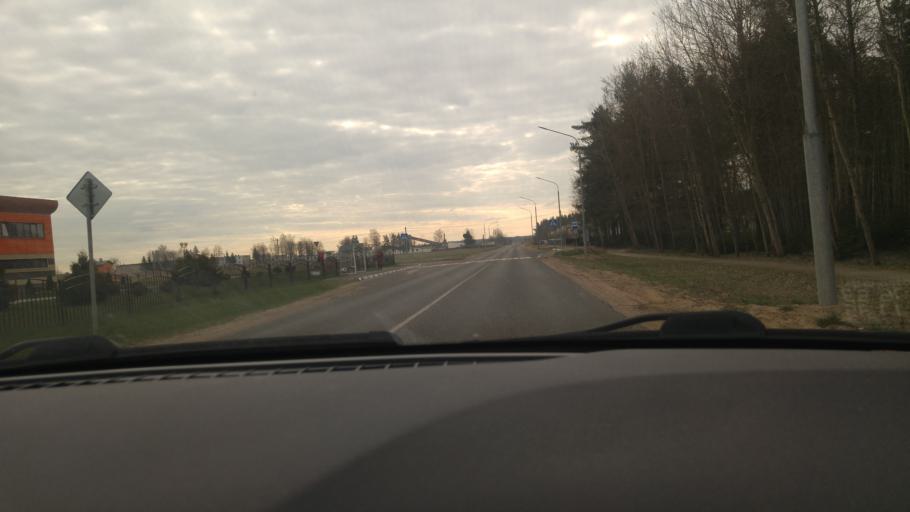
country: BY
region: Minsk
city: Chervyen'
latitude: 53.6997
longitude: 28.4176
